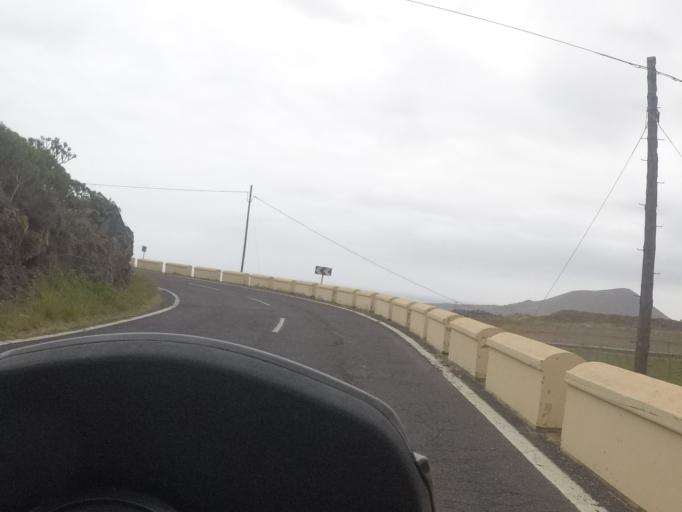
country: ES
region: Canary Islands
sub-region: Provincia de Santa Cruz de Tenerife
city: Candelaria
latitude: 28.3423
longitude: -16.3832
